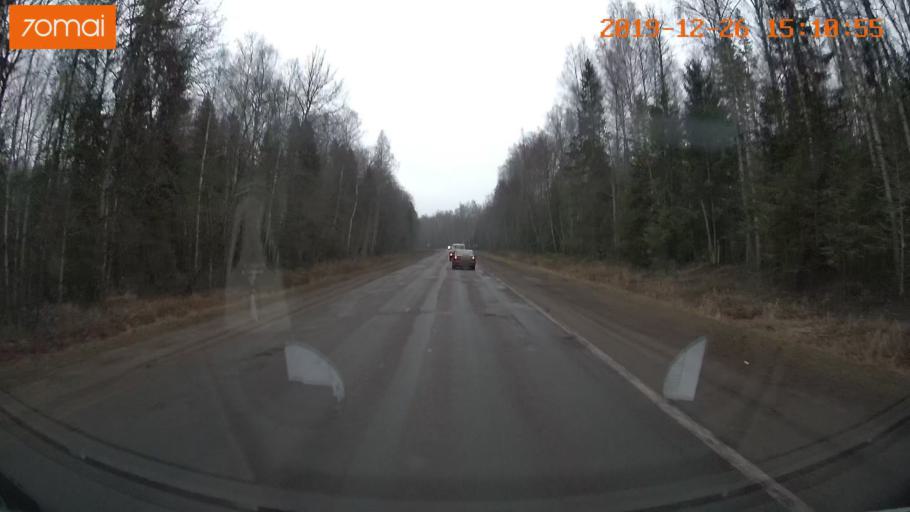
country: RU
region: Jaroslavl
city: Rybinsk
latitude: 58.1372
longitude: 38.8556
